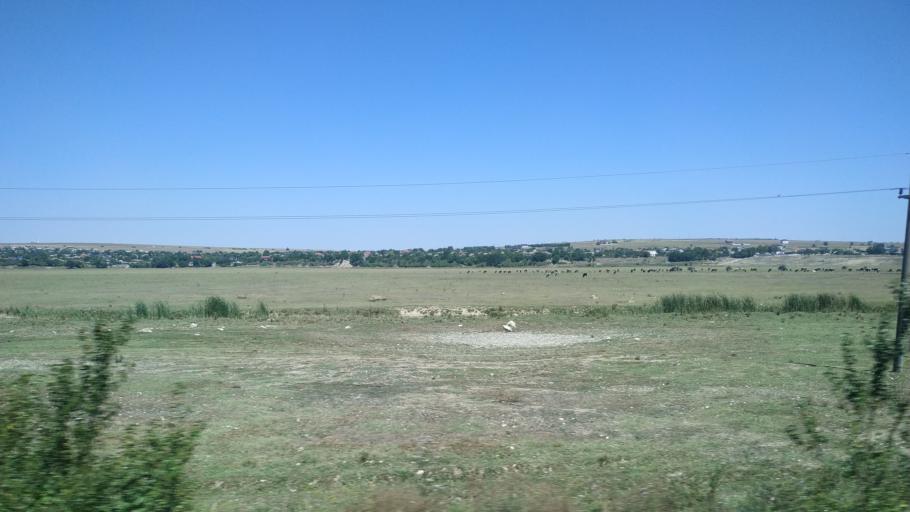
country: RO
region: Constanta
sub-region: Comuna Mircea Voda
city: Satu Nou
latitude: 44.2578
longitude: 28.2268
